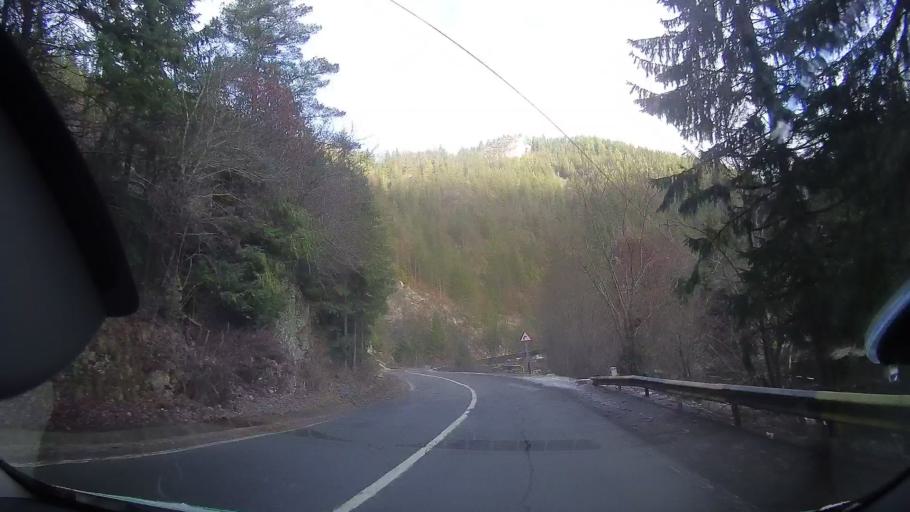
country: RO
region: Alba
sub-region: Comuna Albac
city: Albac
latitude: 46.4553
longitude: 22.9325
